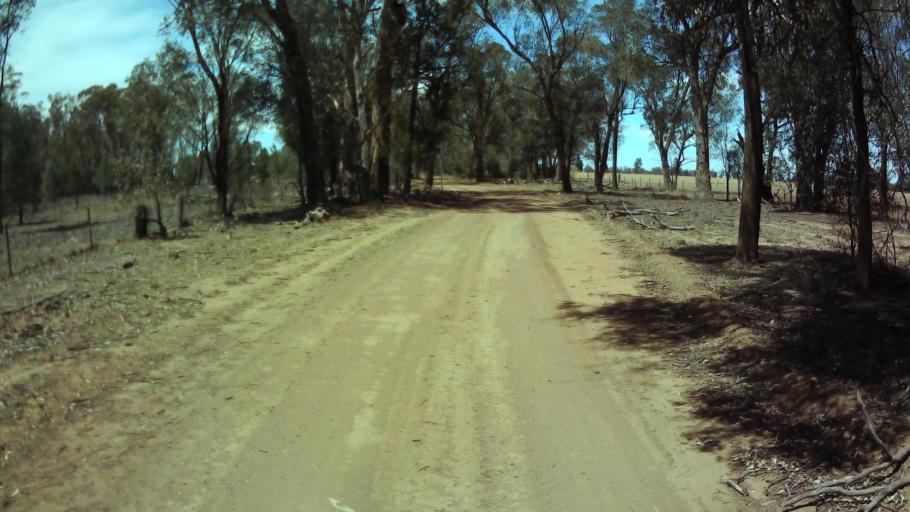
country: AU
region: New South Wales
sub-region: Weddin
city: Grenfell
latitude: -33.9131
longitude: 147.8062
